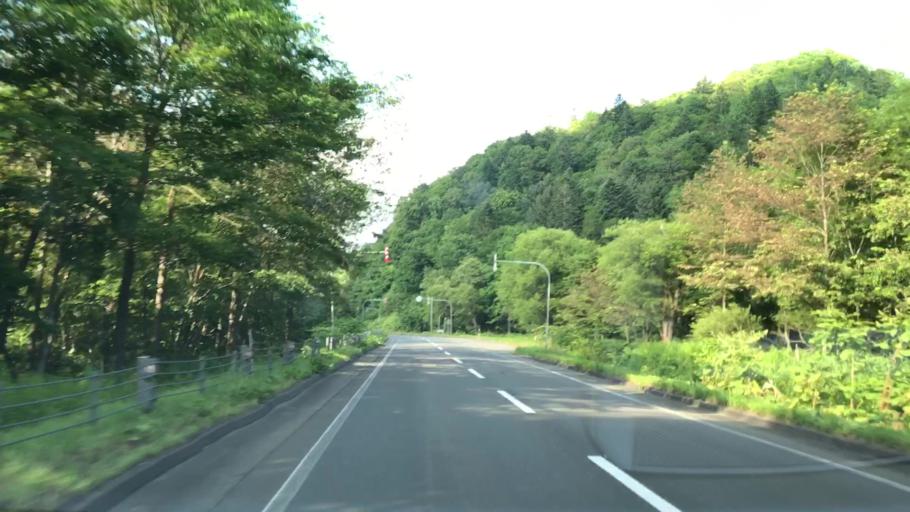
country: JP
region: Hokkaido
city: Iwamizawa
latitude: 42.8926
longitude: 142.1236
